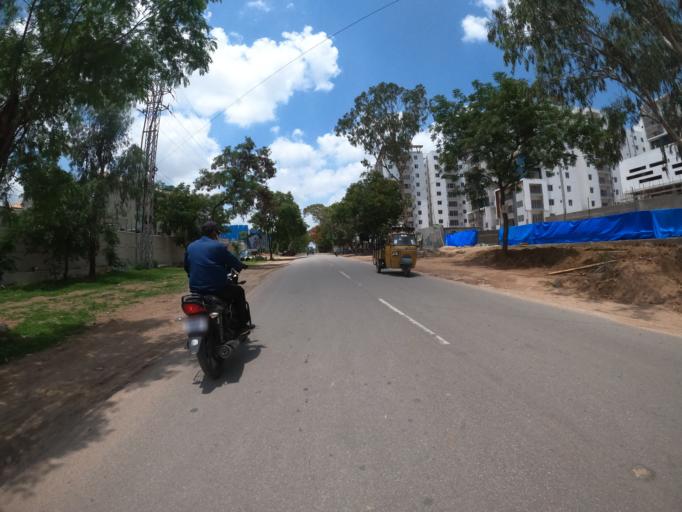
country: IN
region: Telangana
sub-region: Medak
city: Serilingampalle
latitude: 17.3846
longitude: 78.3278
